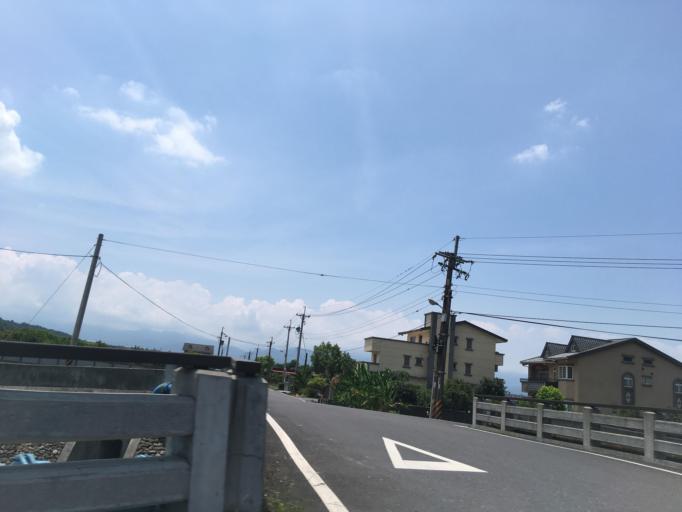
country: TW
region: Taiwan
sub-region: Yilan
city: Yilan
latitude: 24.6416
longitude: 121.7585
